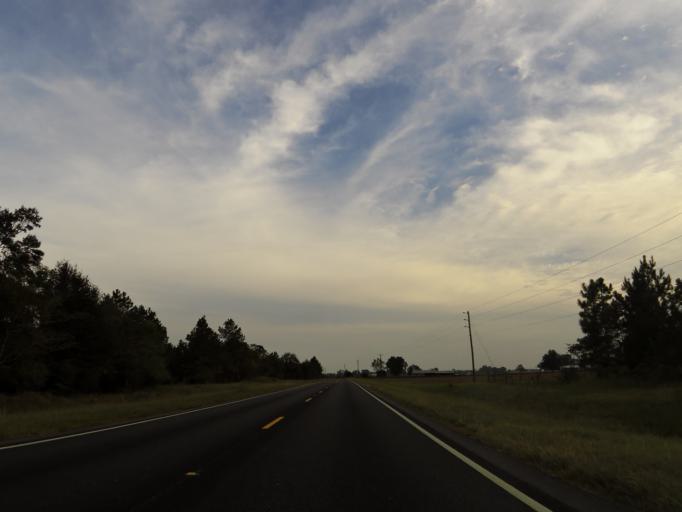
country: US
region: Alabama
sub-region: Escambia County
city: Atmore
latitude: 31.2315
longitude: -87.4802
